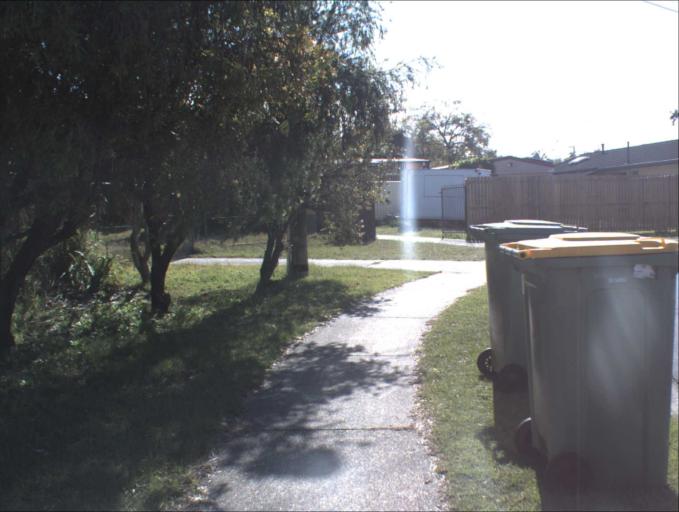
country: AU
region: Queensland
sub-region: Logan
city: Waterford West
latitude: -27.6835
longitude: 153.1050
